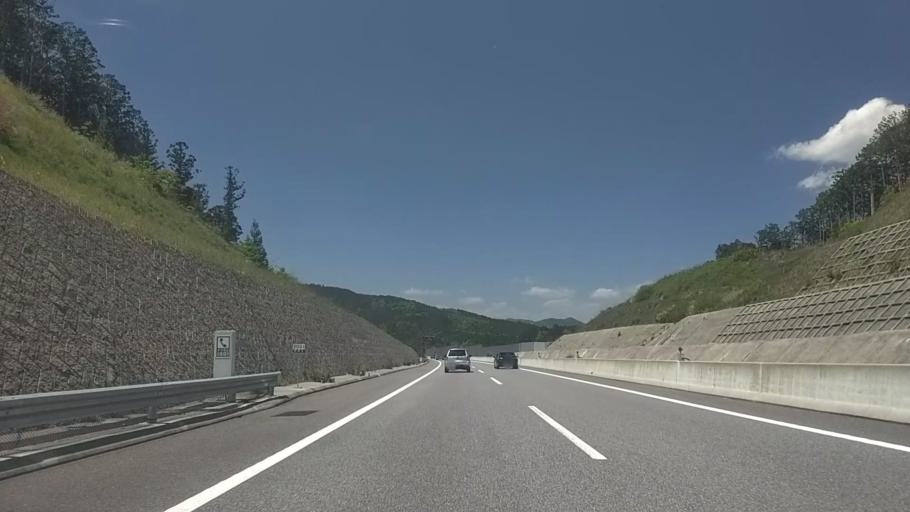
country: JP
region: Aichi
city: Shinshiro
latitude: 34.9061
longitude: 137.6134
